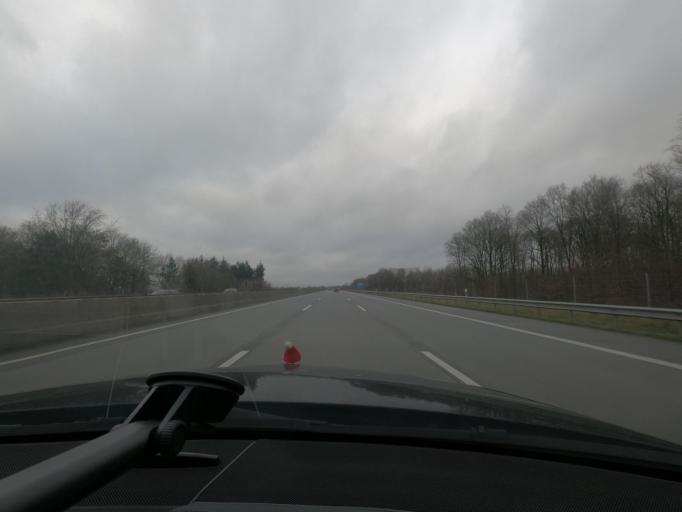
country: DE
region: Schleswig-Holstein
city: Padenstedt
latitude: 54.0224
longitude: 9.9323
